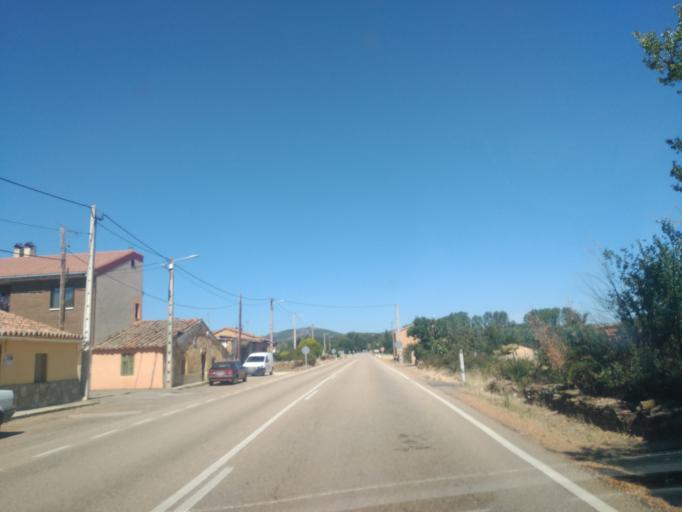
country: ES
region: Castille and Leon
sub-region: Provincia de Zamora
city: Tabara
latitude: 41.8324
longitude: -5.9674
